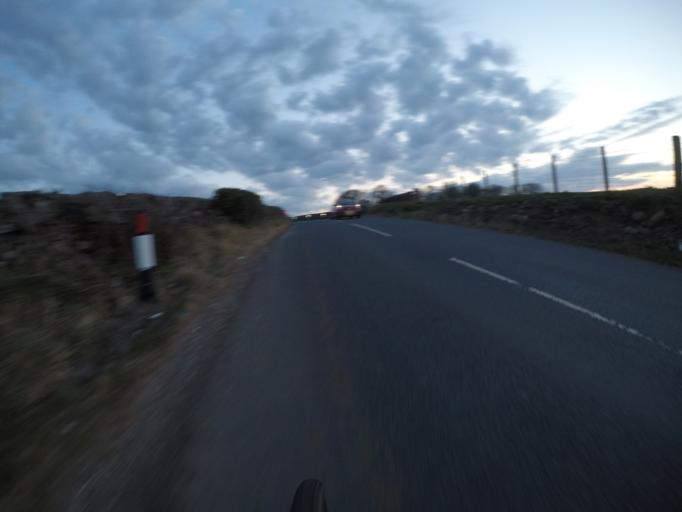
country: GB
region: Scotland
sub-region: South Ayrshire
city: Dundonald
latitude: 55.5626
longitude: -4.6056
